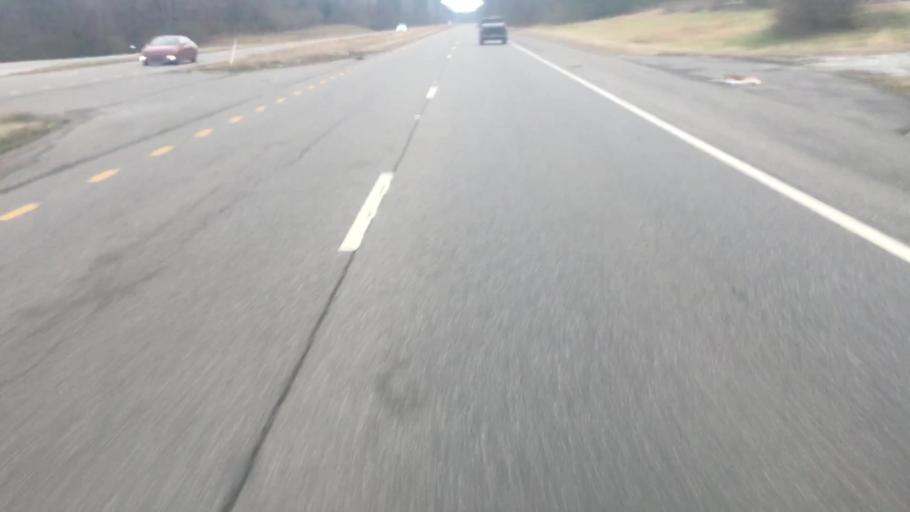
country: US
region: Alabama
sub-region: Walker County
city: Jasper
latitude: 33.8294
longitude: -87.2071
